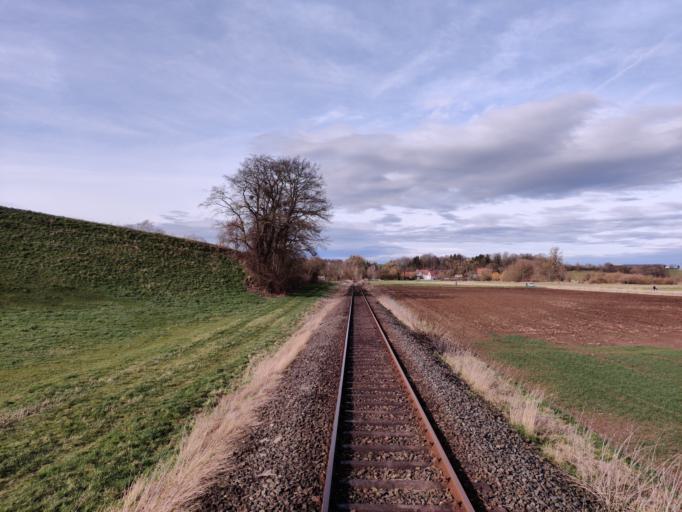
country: DE
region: Lower Saxony
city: Bockenem
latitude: 51.9789
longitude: 10.1225
